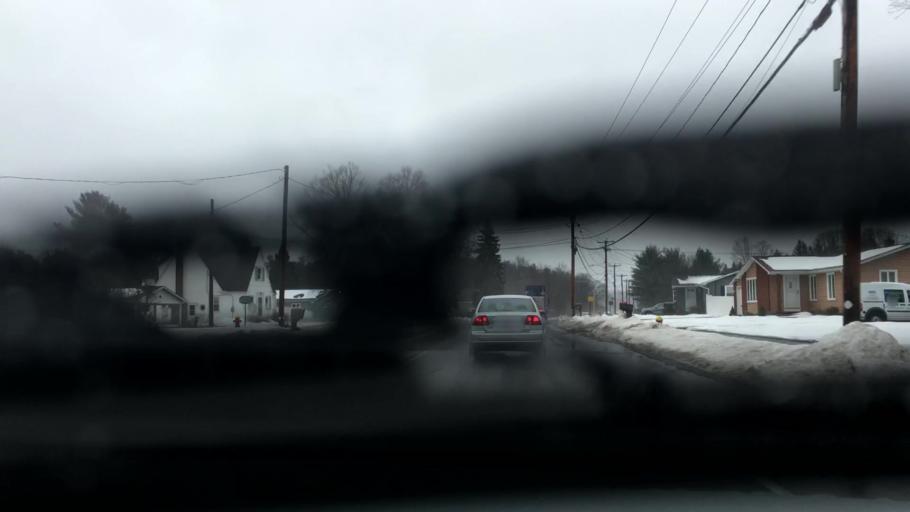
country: US
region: Massachusetts
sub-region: Hampden County
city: Ludlow
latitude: 42.1788
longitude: -72.5208
